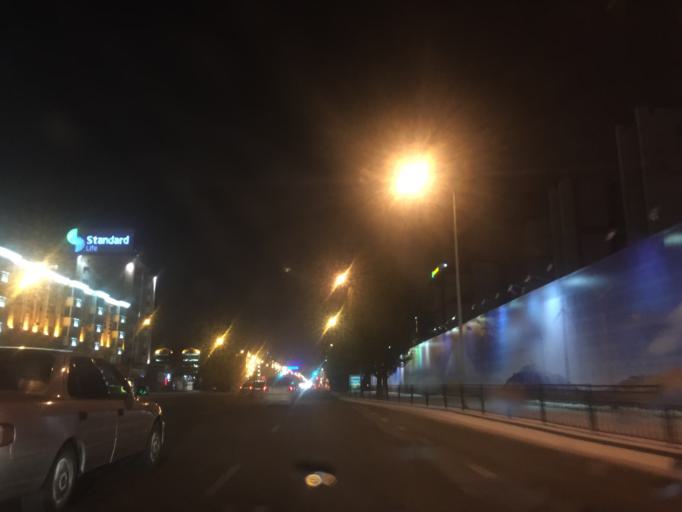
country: KZ
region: Astana Qalasy
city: Astana
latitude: 51.1632
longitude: 71.4282
